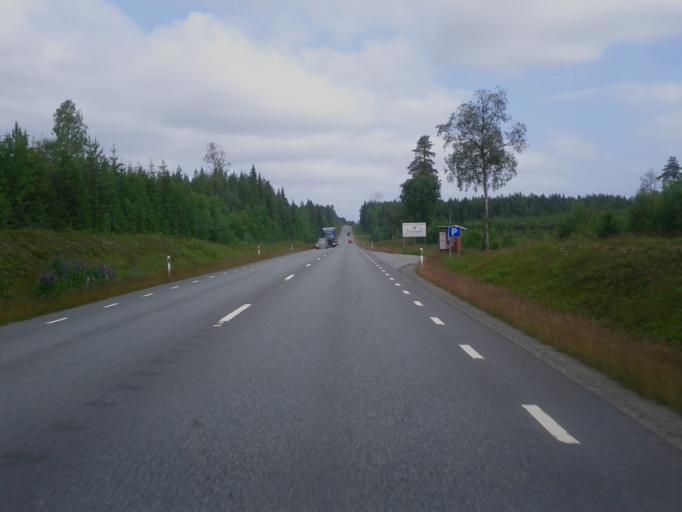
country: SE
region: Vaesterbotten
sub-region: Skelleftea Kommun
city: Burea
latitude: 64.3531
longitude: 21.2940
